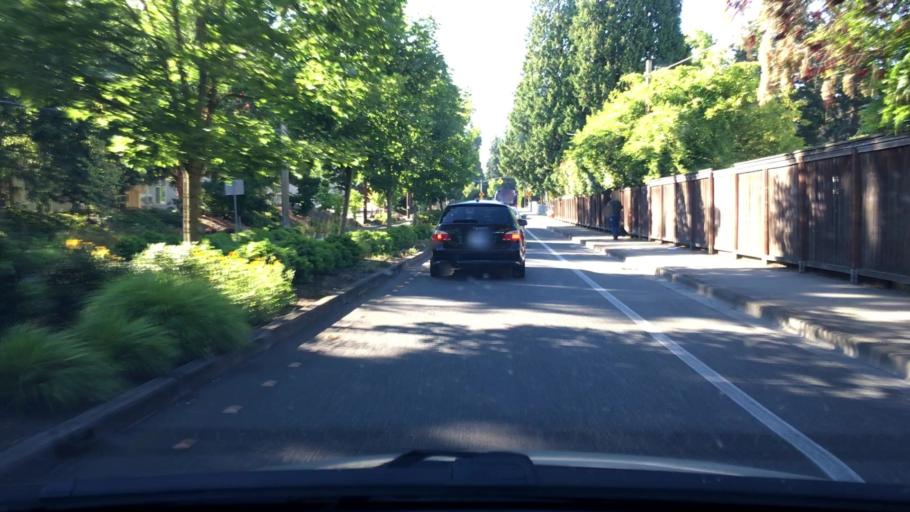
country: US
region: Washington
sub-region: King County
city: Eastgate
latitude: 47.5983
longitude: -122.1513
